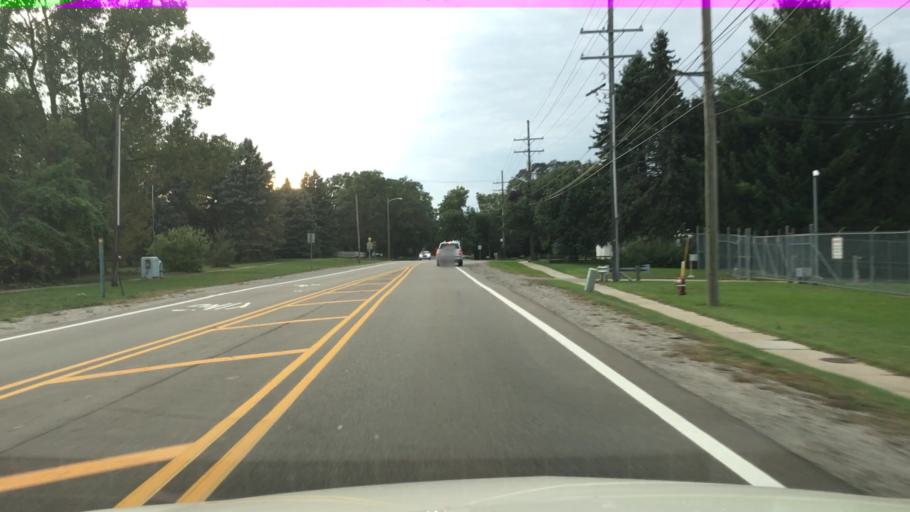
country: US
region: Michigan
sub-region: Oakland County
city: Rochester
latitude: 42.6827
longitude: -83.0844
